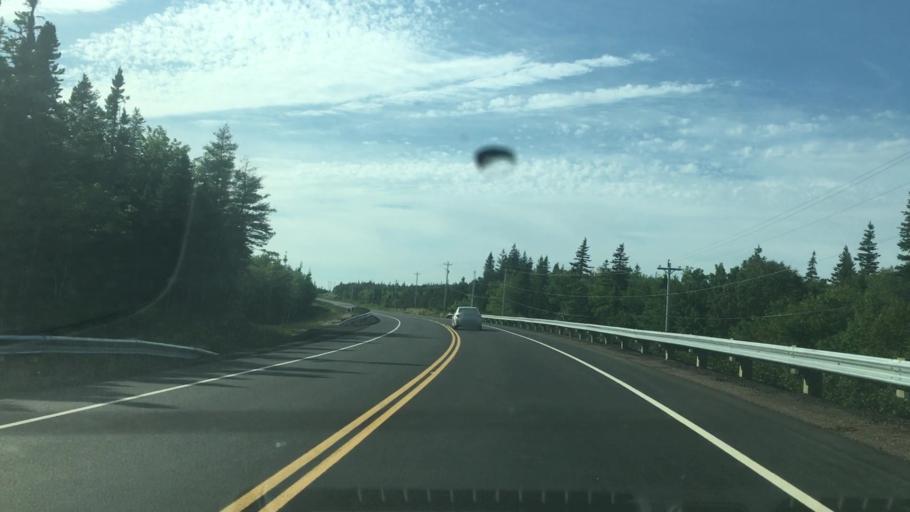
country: CA
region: Nova Scotia
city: Sydney Mines
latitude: 46.8413
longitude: -60.3928
